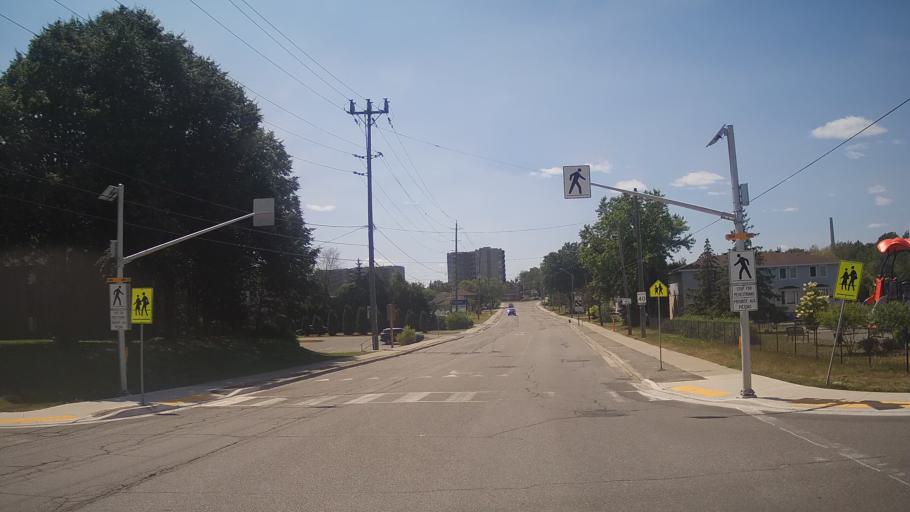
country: CA
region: Ontario
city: Greater Sudbury
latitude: 46.4639
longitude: -81.0031
